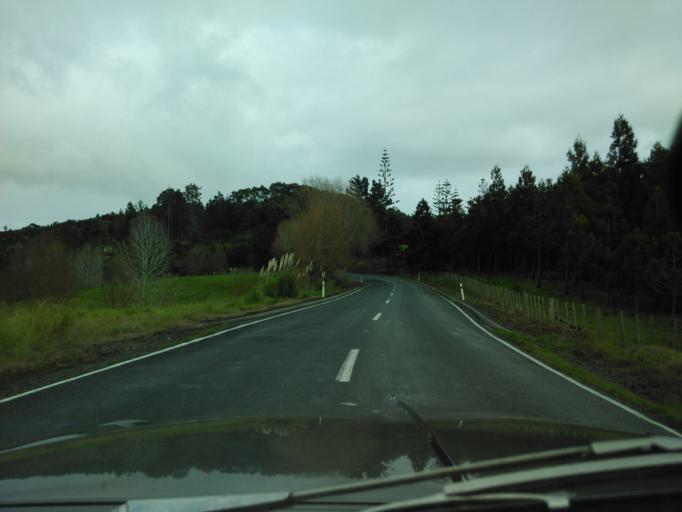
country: NZ
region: Auckland
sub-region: Auckland
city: Wellsford
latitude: -36.3315
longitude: 174.3846
